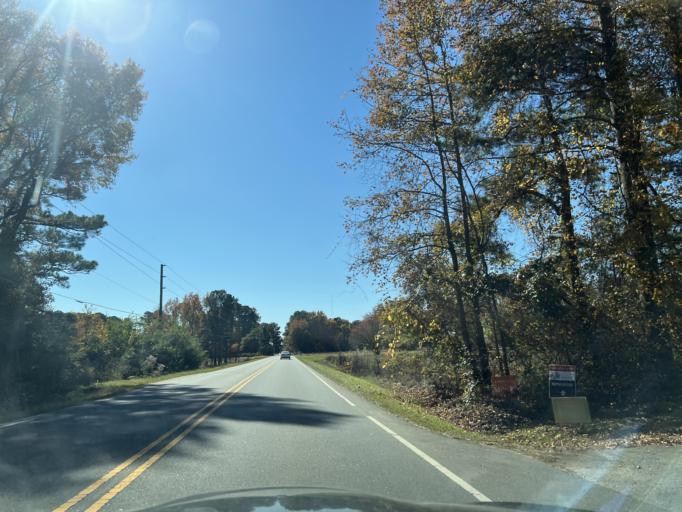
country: US
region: North Carolina
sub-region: Wake County
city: Fuquay-Varina
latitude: 35.6554
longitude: -78.7183
